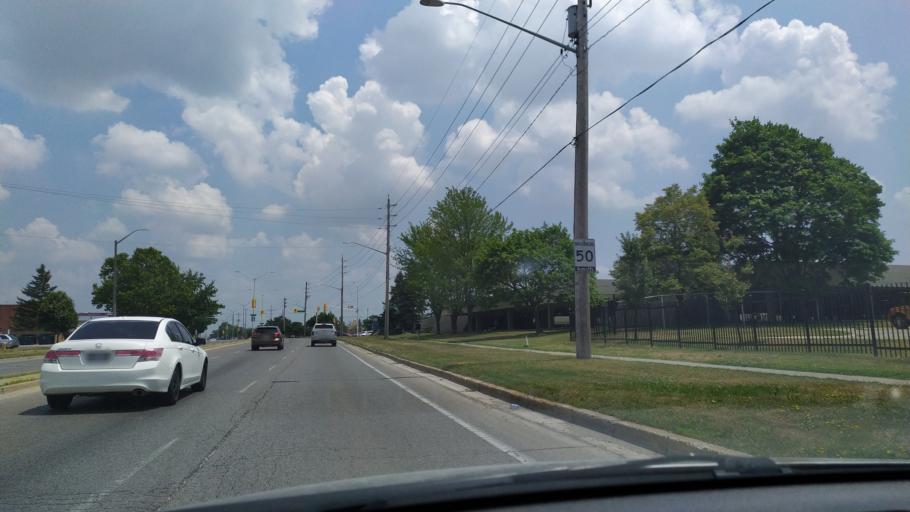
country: CA
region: Ontario
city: London
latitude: 42.9342
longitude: -81.2275
